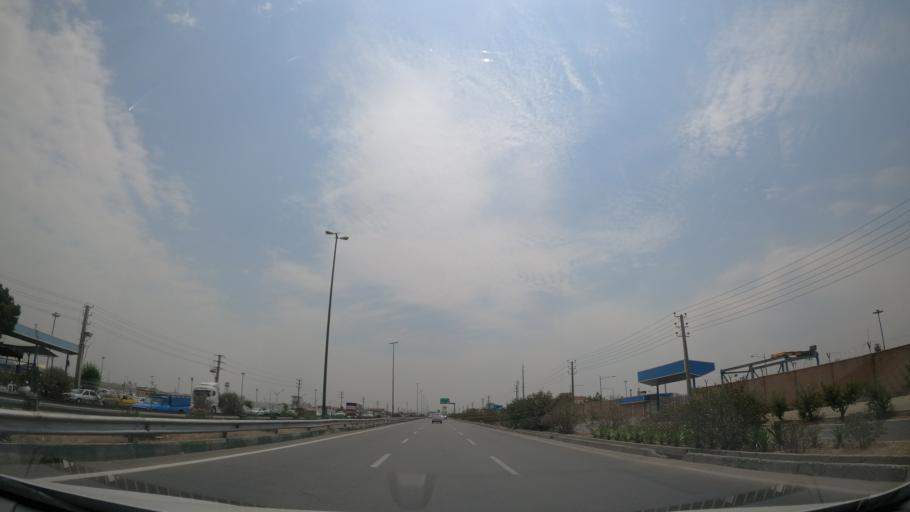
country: IR
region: Tehran
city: Shahr-e Qods
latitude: 35.6995
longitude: 51.1933
